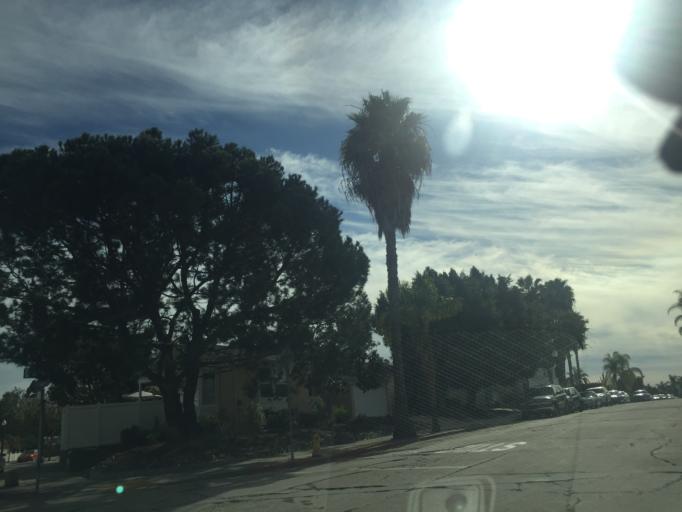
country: US
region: California
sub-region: San Diego County
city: Lemon Grove
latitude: 32.7605
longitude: -117.0838
